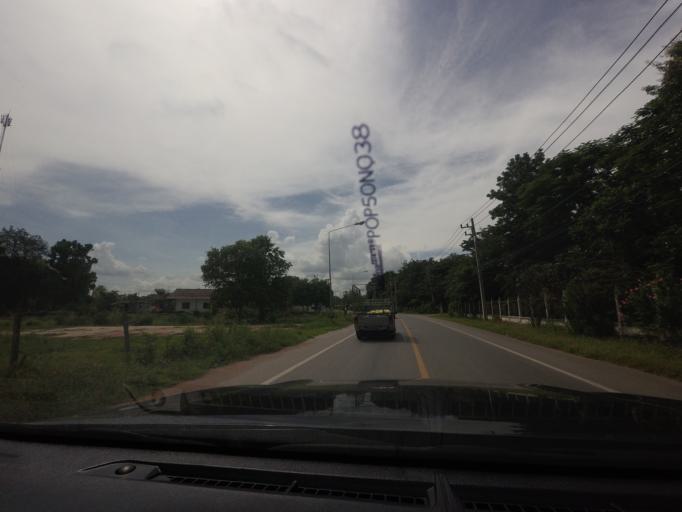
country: TH
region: Kanchanaburi
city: Phanom Thuan
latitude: 14.1047
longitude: 99.6561
